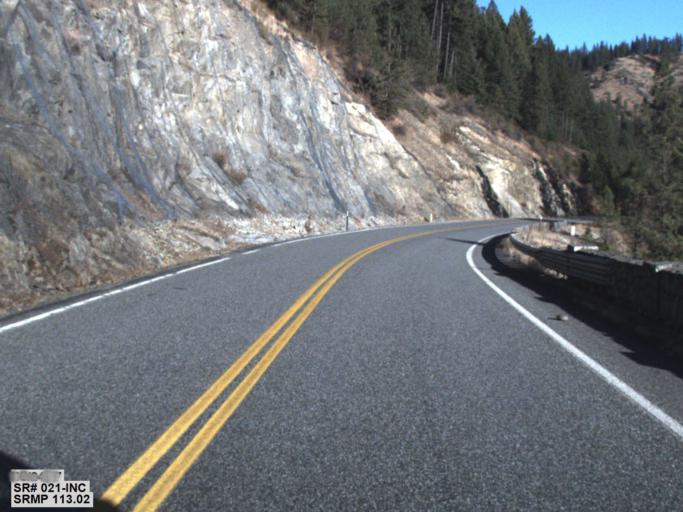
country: US
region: Washington
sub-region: Okanogan County
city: Coulee Dam
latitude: 48.0292
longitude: -118.6739
